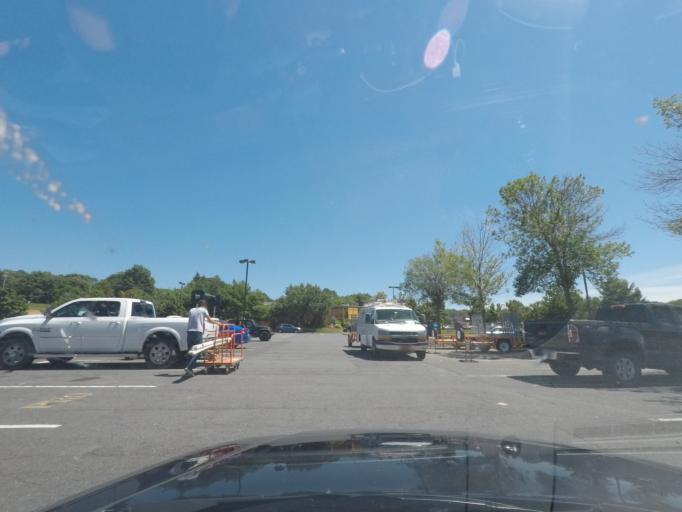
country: US
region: New York
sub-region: Rensselaer County
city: Hampton Manor
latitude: 42.6472
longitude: -73.6993
